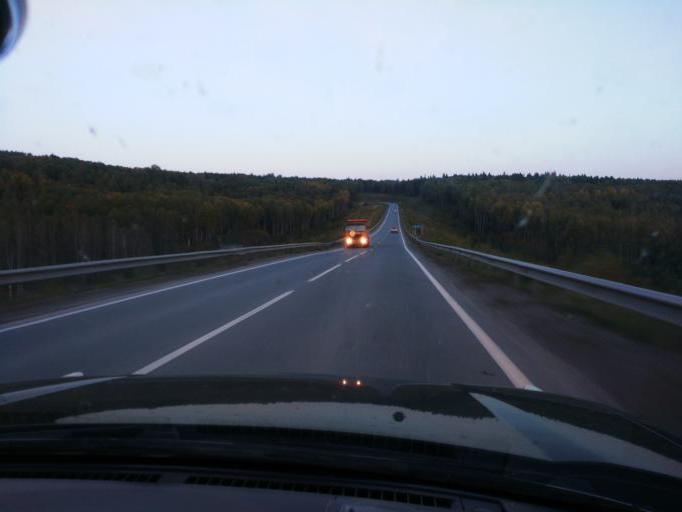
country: RU
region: Perm
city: Sylva
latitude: 58.3003
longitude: 56.7927
